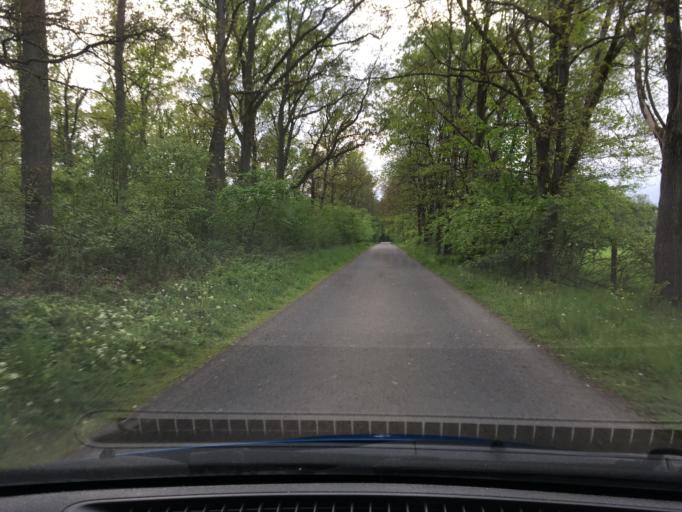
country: DE
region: Lower Saxony
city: Fassberg
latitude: 52.9598
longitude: 10.1932
